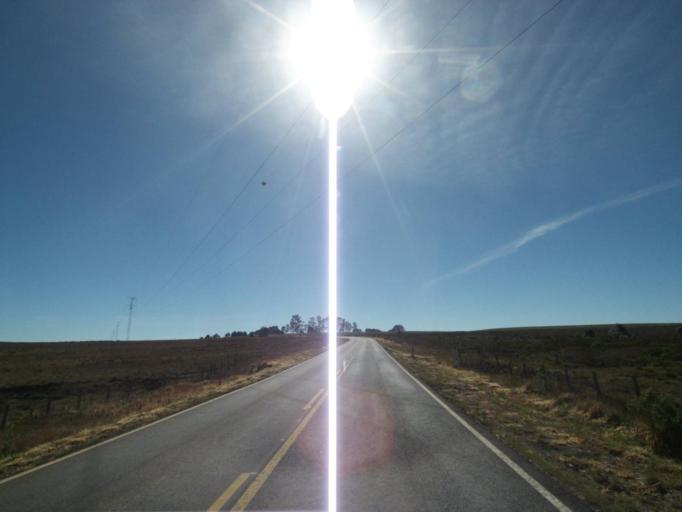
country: BR
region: Parana
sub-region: Castro
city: Castro
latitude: -24.6798
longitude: -50.2133
